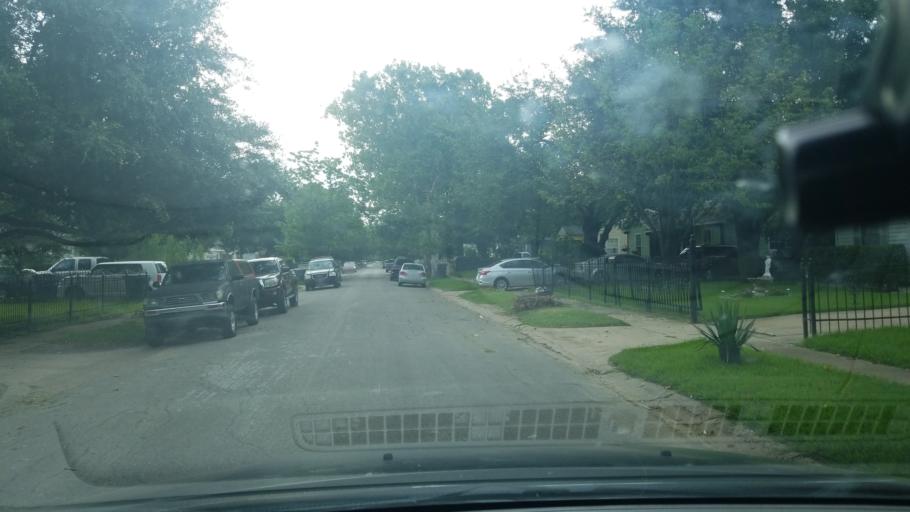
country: US
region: Texas
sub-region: Dallas County
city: Balch Springs
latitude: 32.7387
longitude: -96.6712
